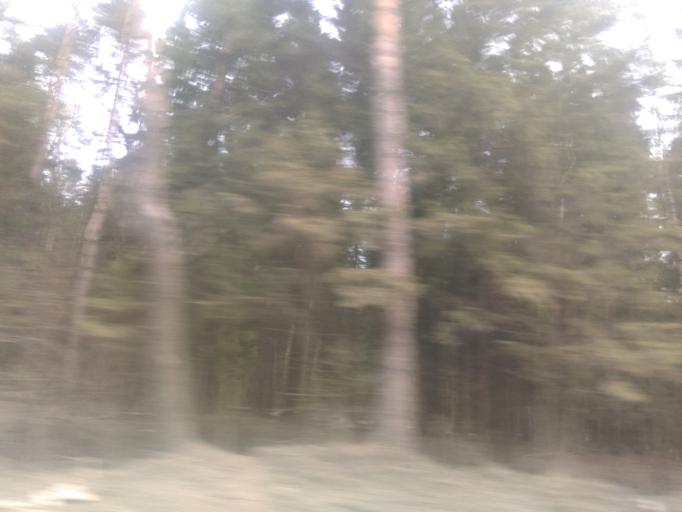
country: RU
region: Moskovskaya
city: Tuchkovo
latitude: 55.5658
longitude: 36.5250
